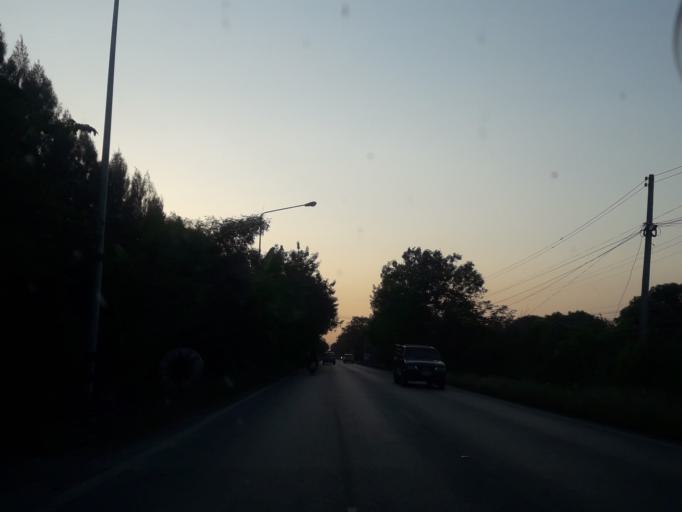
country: TH
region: Pathum Thani
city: Nong Suea
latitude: 14.1313
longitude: 100.7740
